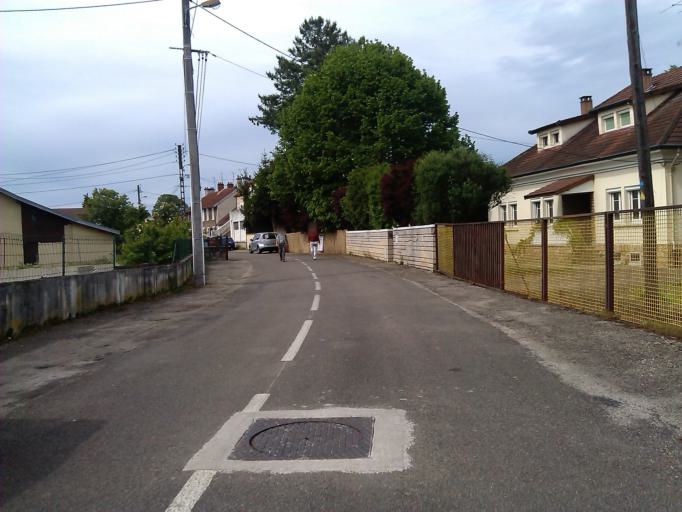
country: FR
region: Franche-Comte
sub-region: Departement du Jura
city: Dole
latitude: 47.1015
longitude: 5.4978
